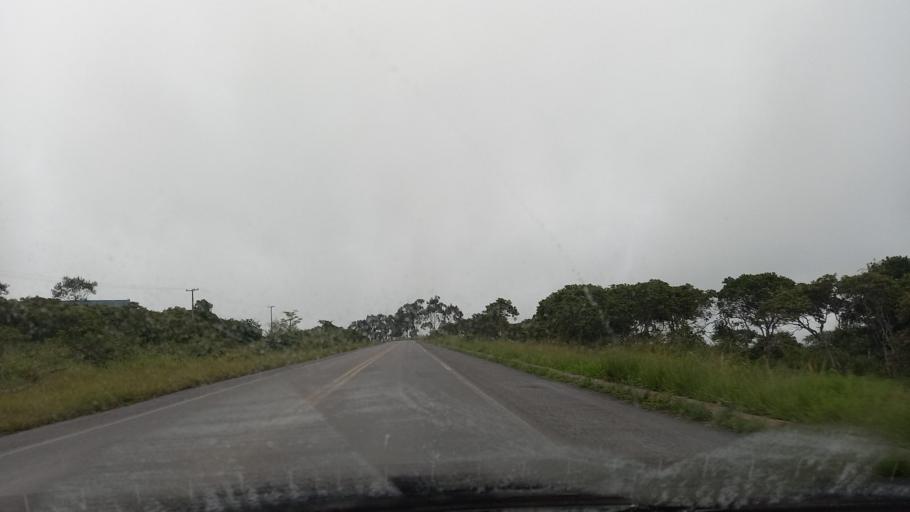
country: BR
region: Pernambuco
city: Garanhuns
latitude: -8.8732
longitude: -36.5340
